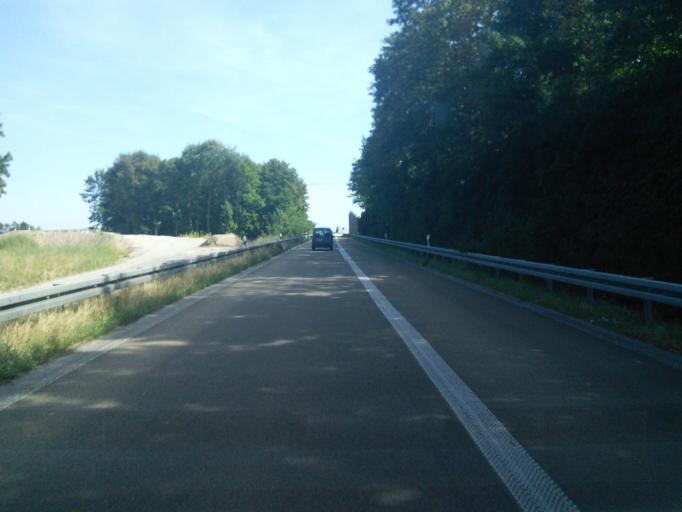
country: DE
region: North Rhine-Westphalia
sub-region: Regierungsbezirk Dusseldorf
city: Kaarst
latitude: 51.2324
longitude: 6.6359
